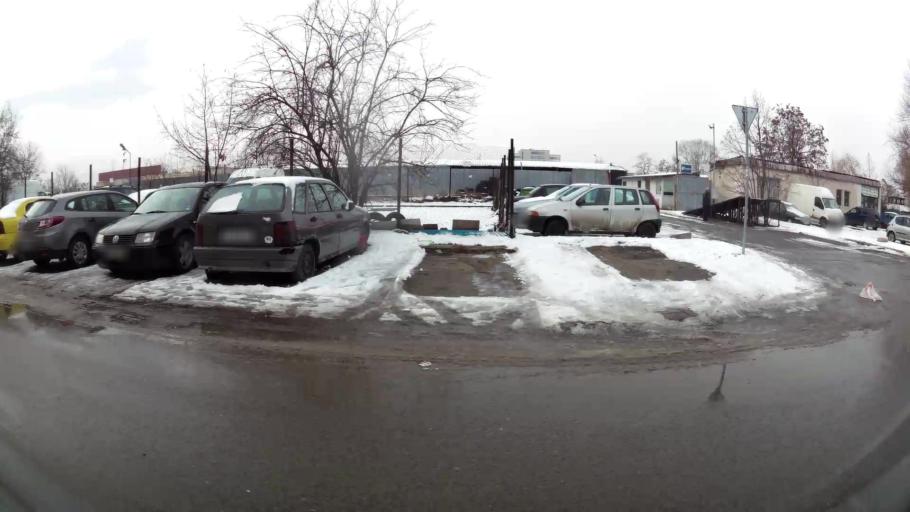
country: BG
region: Sofia-Capital
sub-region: Stolichna Obshtina
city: Sofia
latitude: 42.7116
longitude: 23.3755
